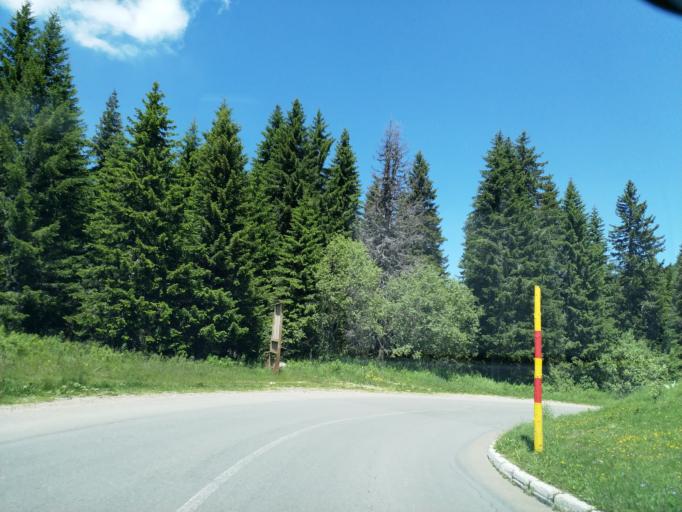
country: XK
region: Mitrovica
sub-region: Komuna e Leposaviqit
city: Leposaviq
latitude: 43.2887
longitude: 20.8134
